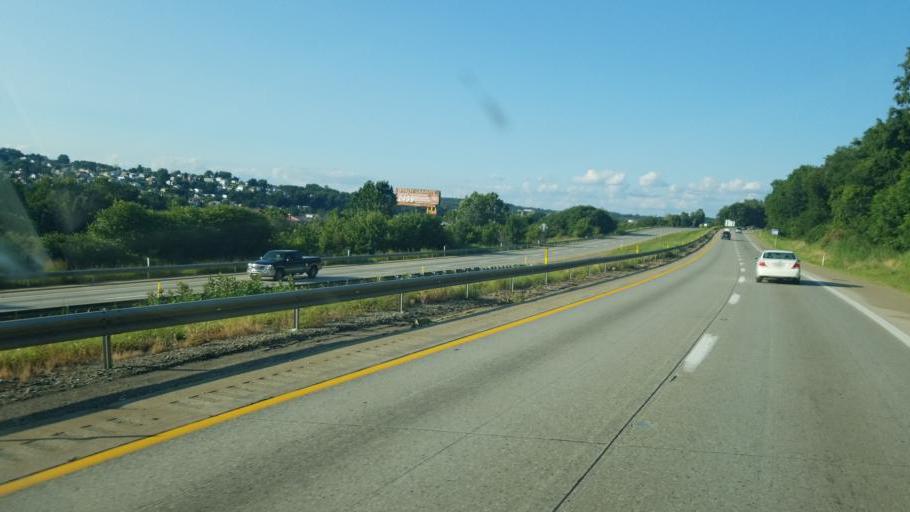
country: US
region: Pennsylvania
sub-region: Washington County
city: Canonsburg
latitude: 40.2598
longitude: -80.1737
